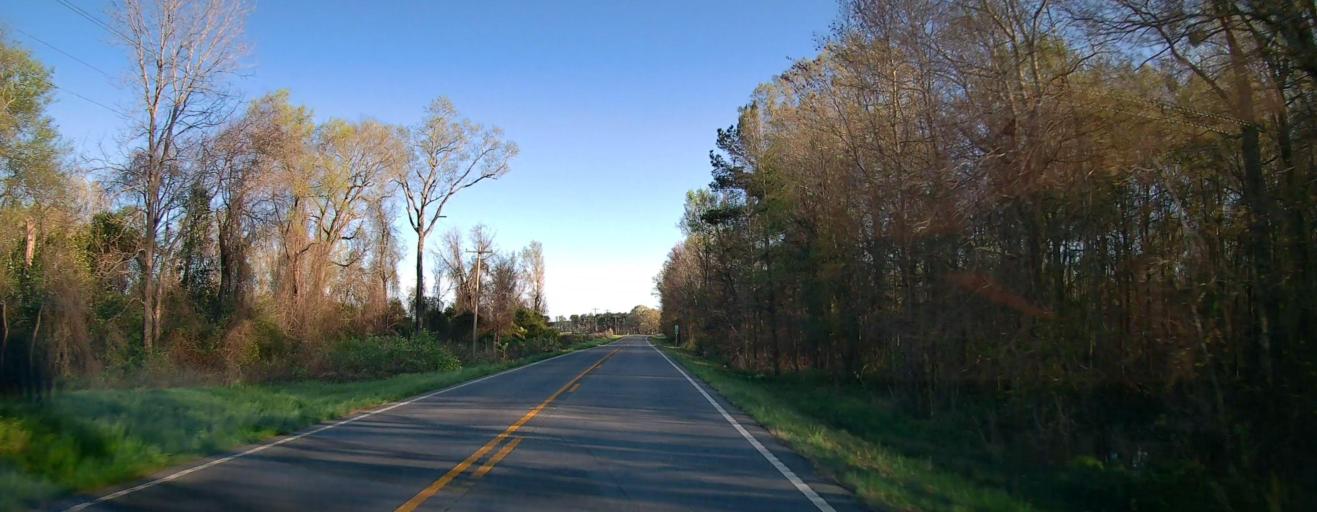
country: US
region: Georgia
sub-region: Pulaski County
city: Hawkinsville
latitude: 32.2211
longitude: -83.3882
